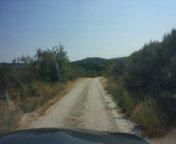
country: PT
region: Viseu
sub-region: Sernancelhe
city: Sernancelhe
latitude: 40.9322
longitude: -7.5125
